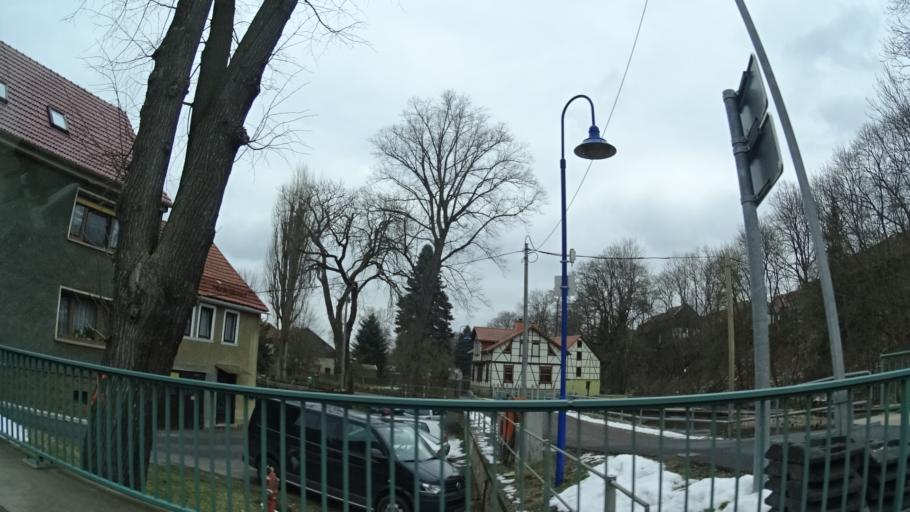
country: DE
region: Thuringia
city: Pennewitz
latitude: 50.7006
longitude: 11.0203
